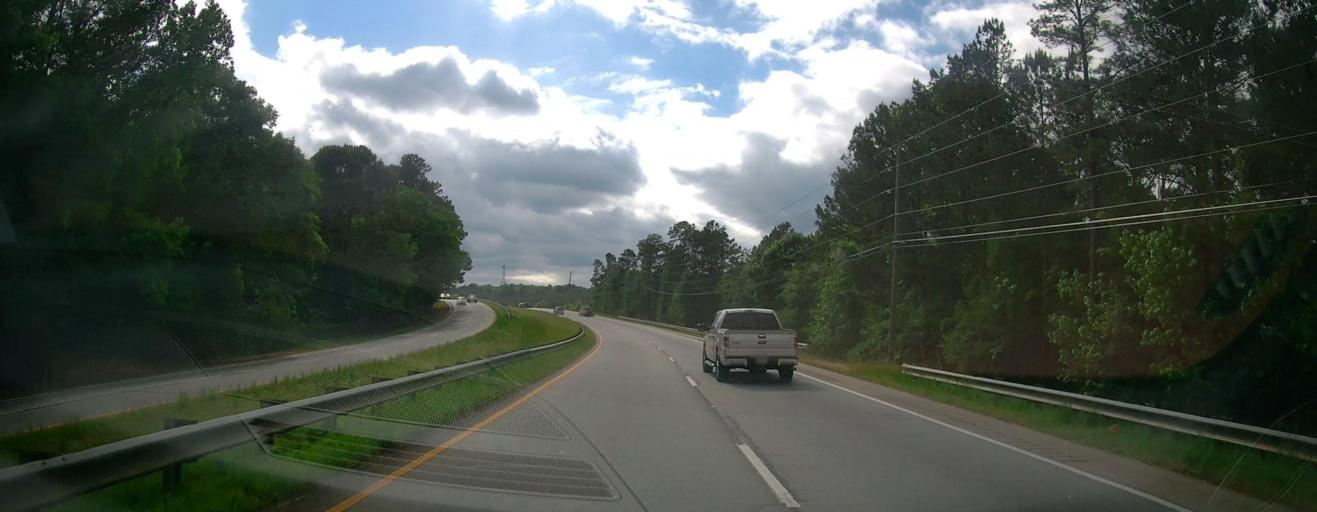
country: US
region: Georgia
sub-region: Walton County
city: Monroe
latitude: 33.8068
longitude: -83.7682
